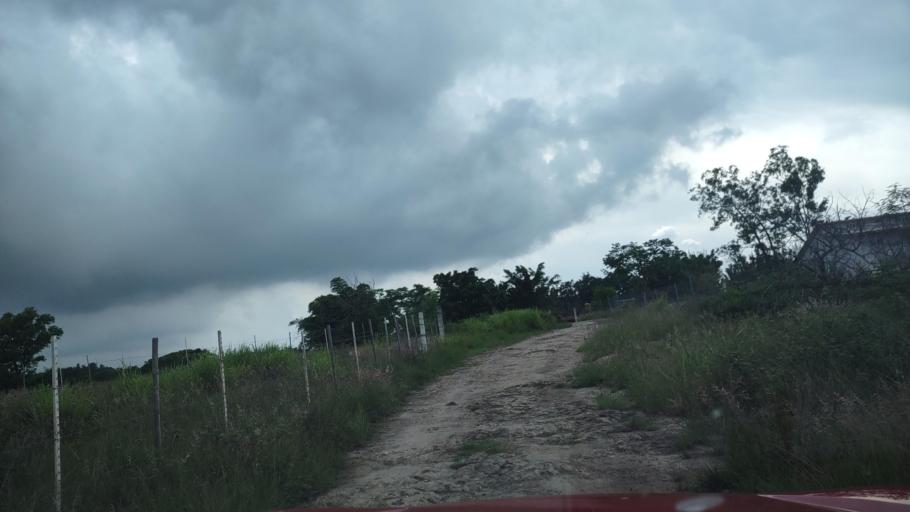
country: MX
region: Veracruz
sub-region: Emiliano Zapata
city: Dos Rios
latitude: 19.4760
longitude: -96.8173
